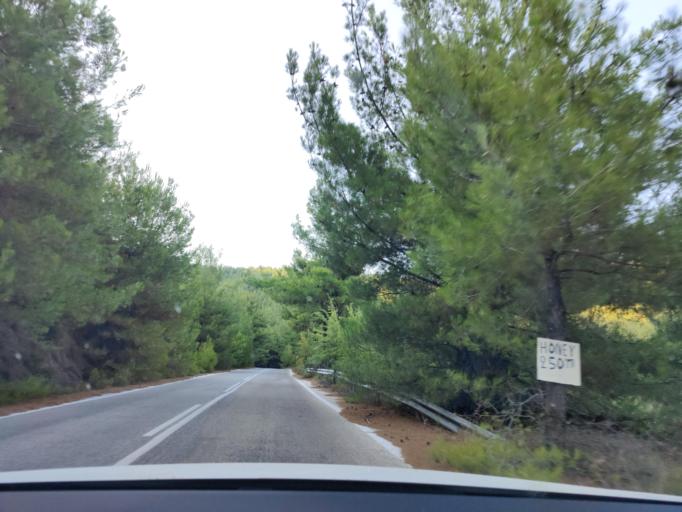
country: GR
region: East Macedonia and Thrace
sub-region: Nomos Kavalas
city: Potamia
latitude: 40.6265
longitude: 24.7645
